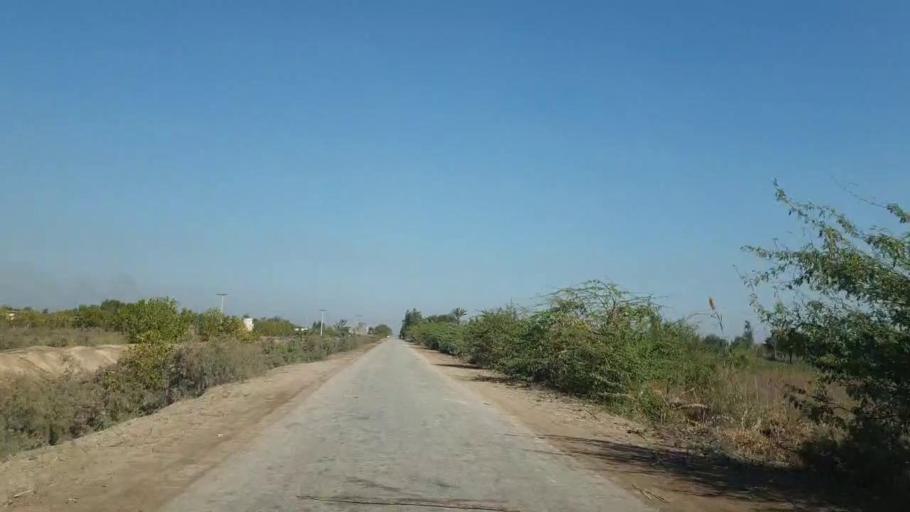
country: PK
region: Sindh
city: Mirpur Khas
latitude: 25.5761
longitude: 69.0461
